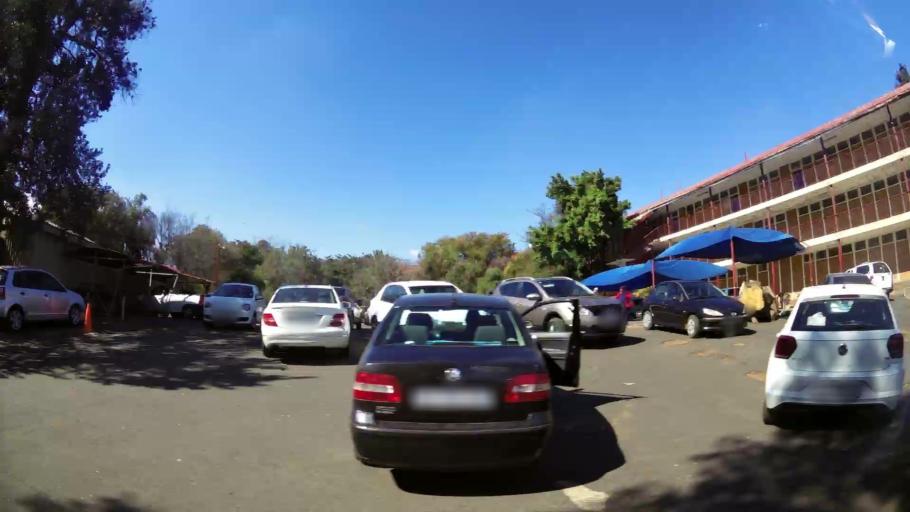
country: ZA
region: Mpumalanga
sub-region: Nkangala District Municipality
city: Witbank
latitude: -25.8705
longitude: 29.2158
